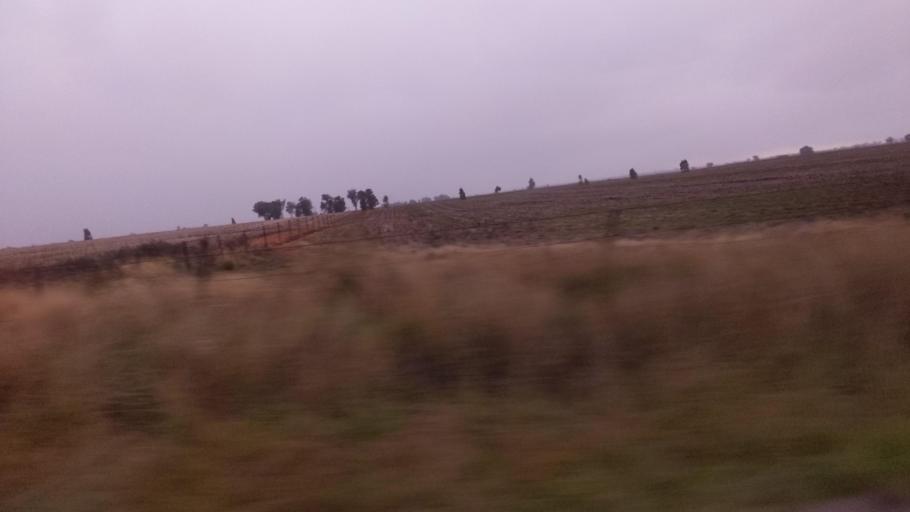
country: AU
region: New South Wales
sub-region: Narrandera
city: Narrandera
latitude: -34.7446
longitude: 146.8063
